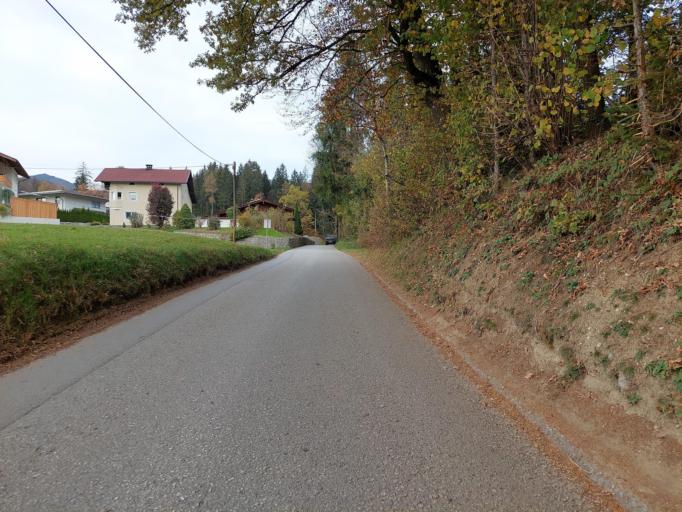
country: AT
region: Tyrol
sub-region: Politischer Bezirk Kufstein
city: Angath
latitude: 47.4991
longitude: 12.0485
